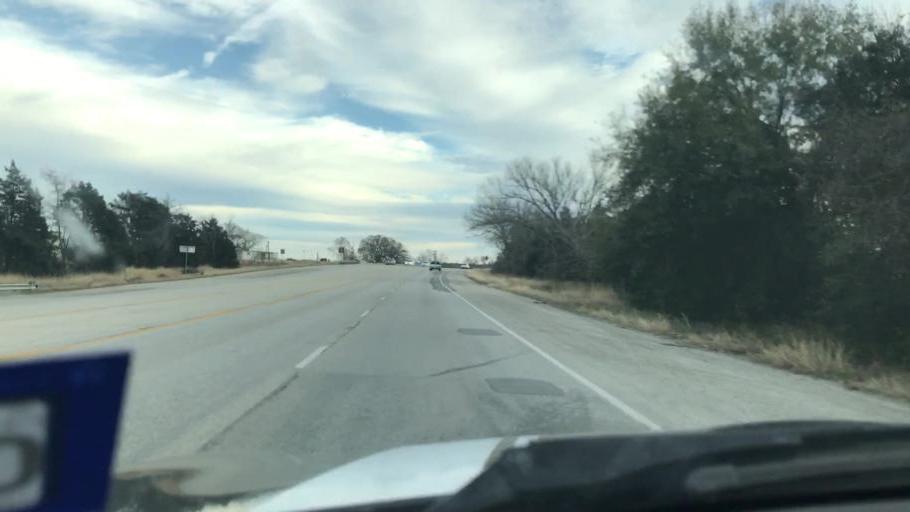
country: US
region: Texas
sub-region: Bastrop County
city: Camp Swift
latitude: 30.2870
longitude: -97.2482
